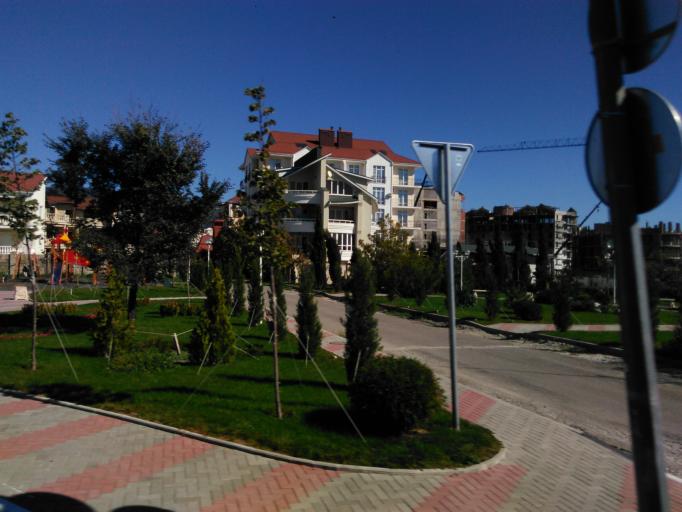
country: RU
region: Krasnodarskiy
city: Gelendzhik
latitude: 44.5491
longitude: 38.0542
